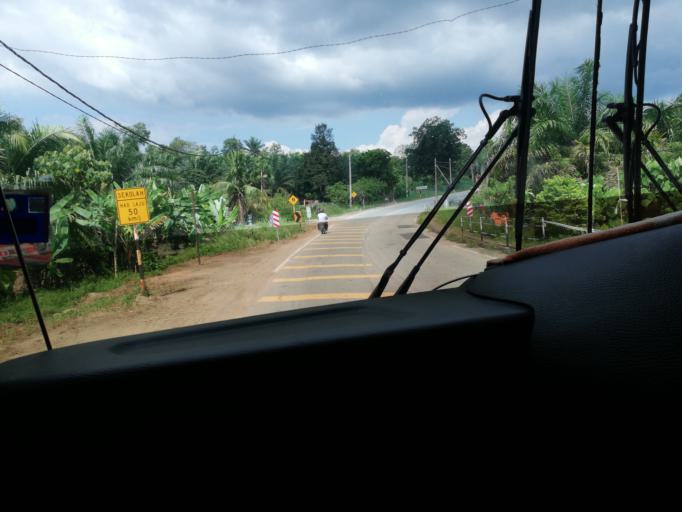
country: MY
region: Perak
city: Parit Buntar
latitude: 5.1373
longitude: 100.5861
